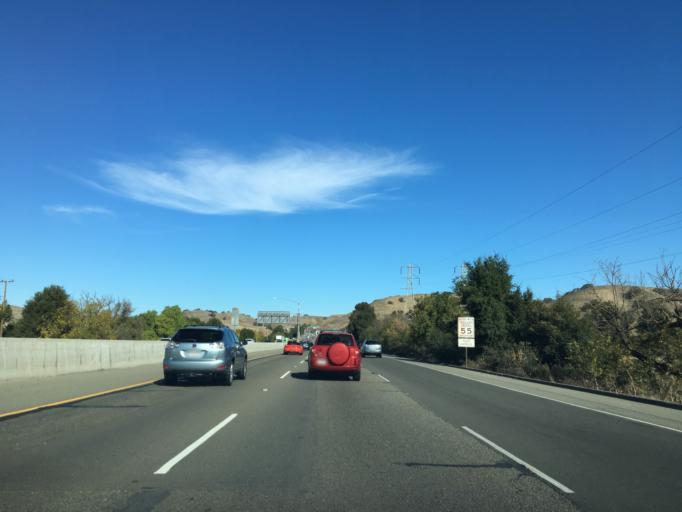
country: US
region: California
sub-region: Alameda County
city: Pleasanton
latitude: 37.5822
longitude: -121.8742
